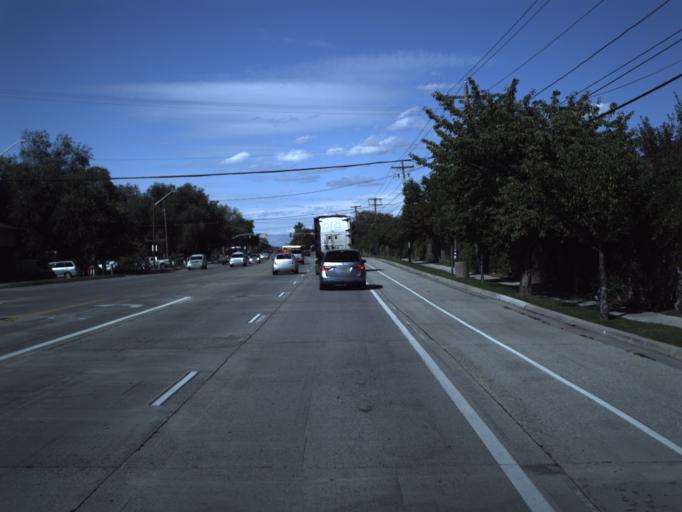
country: US
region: Utah
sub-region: Salt Lake County
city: Salt Lake City
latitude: 40.7886
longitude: -111.9392
